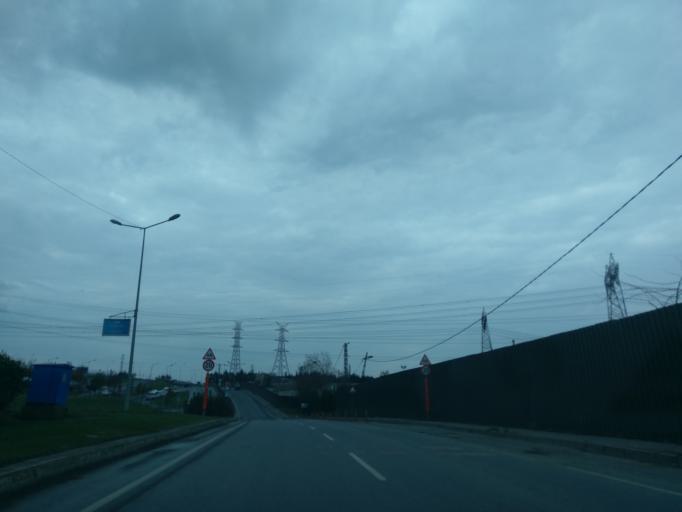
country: TR
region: Istanbul
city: Sisli
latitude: 41.1008
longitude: 28.9620
